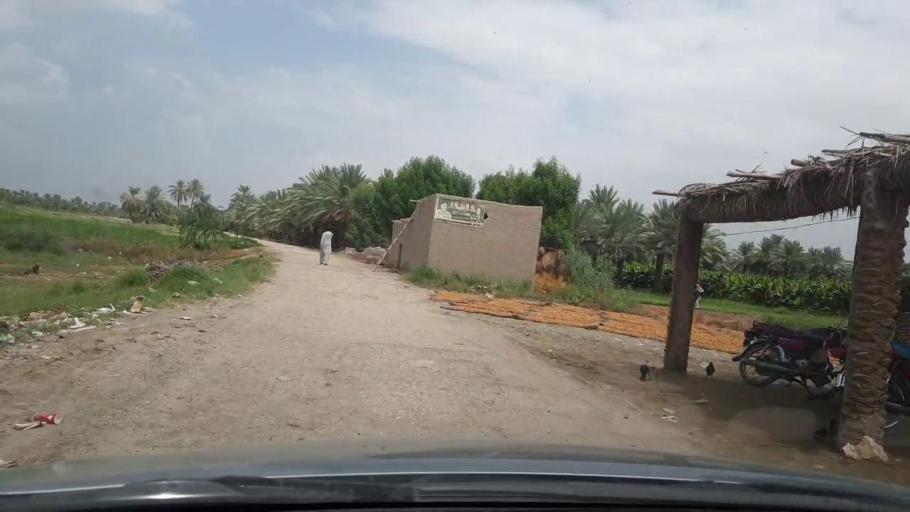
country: PK
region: Sindh
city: Kot Diji
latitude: 27.4122
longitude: 68.7458
